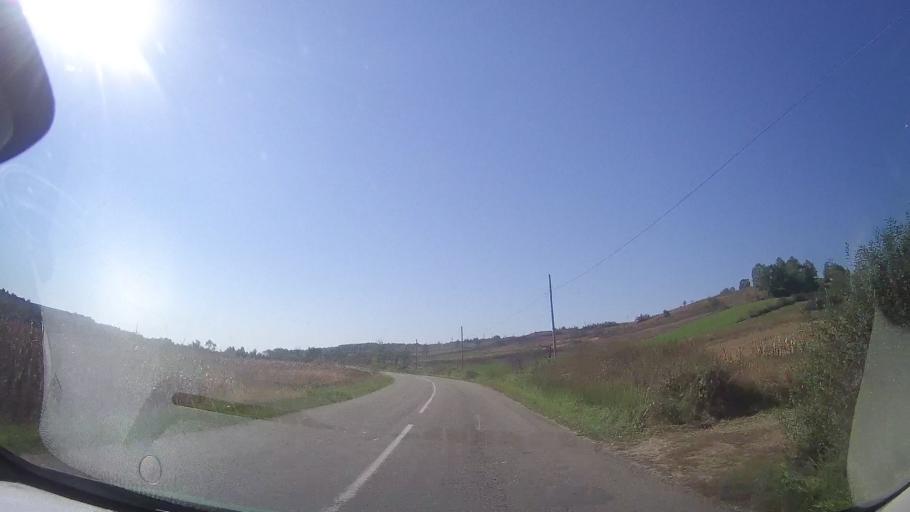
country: RO
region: Timis
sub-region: Comuna Ohaba Lunga
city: Ohaba Lunga
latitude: 45.8997
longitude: 21.9757
